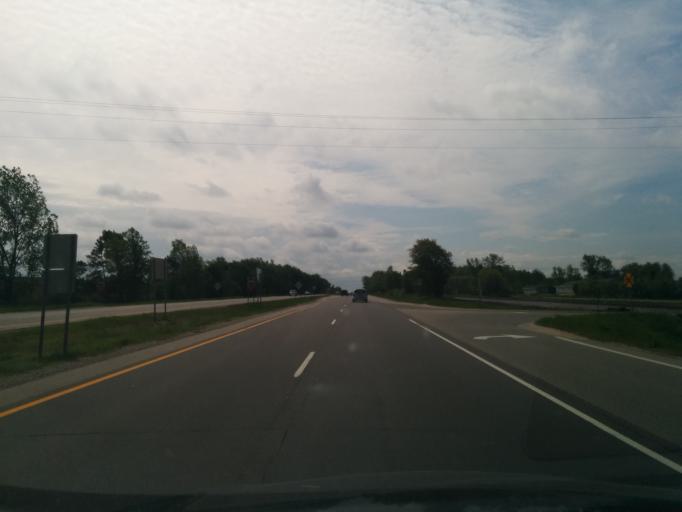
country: US
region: Michigan
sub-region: Ottawa County
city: Beechwood
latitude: 42.9107
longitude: -86.1413
